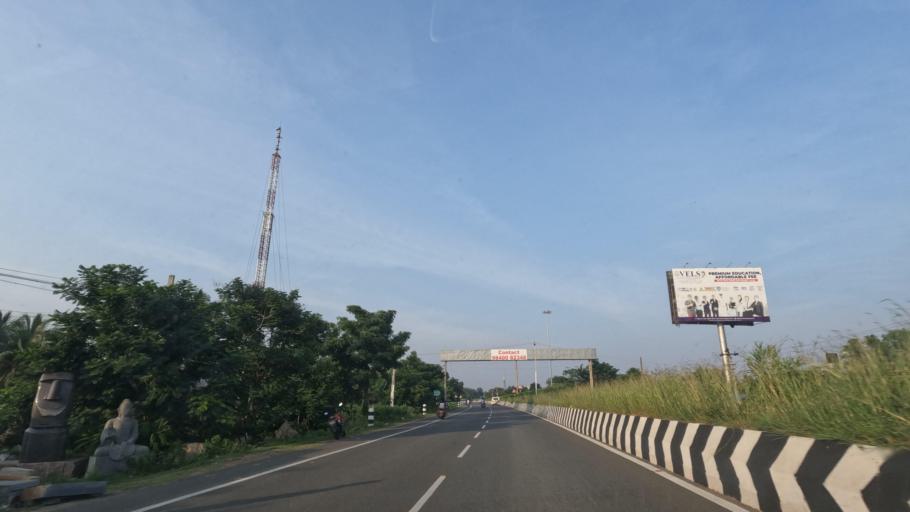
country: IN
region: Tamil Nadu
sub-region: Kancheepuram
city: Mamallapuram
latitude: 12.6476
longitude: 80.2027
